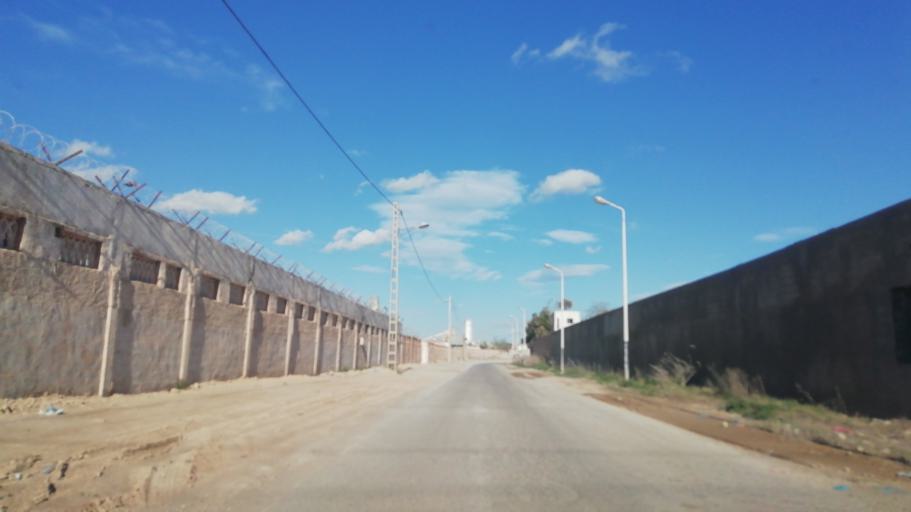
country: DZ
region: Oran
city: Sidi ech Chahmi
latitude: 35.6389
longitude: -0.5468
